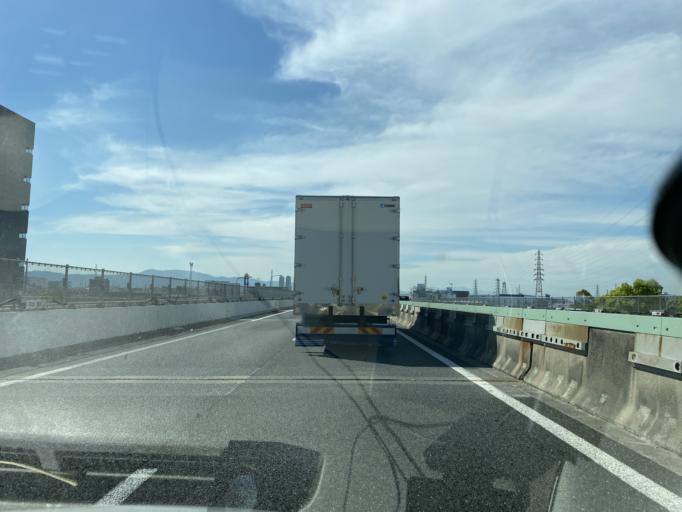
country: JP
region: Osaka
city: Kadoma
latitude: 34.7755
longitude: 135.5618
